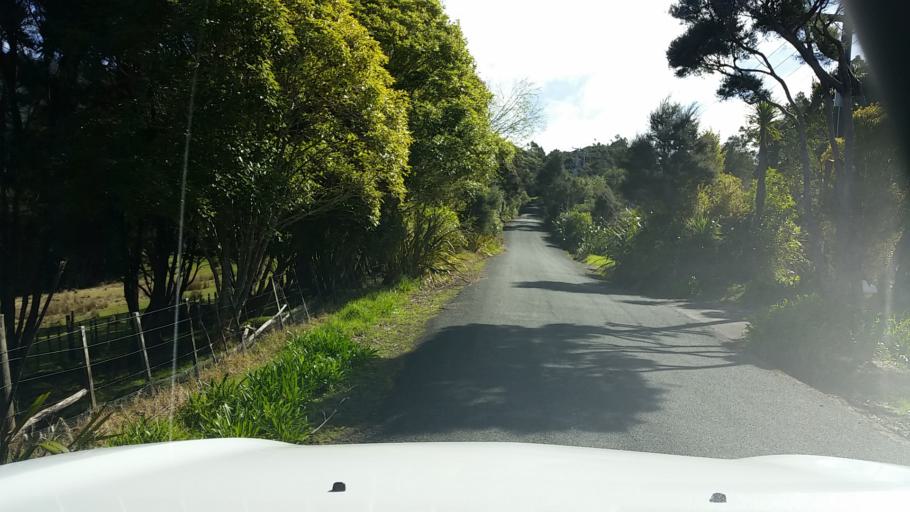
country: NZ
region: Auckland
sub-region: Auckland
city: Titirangi
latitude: -36.9812
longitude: 174.6121
